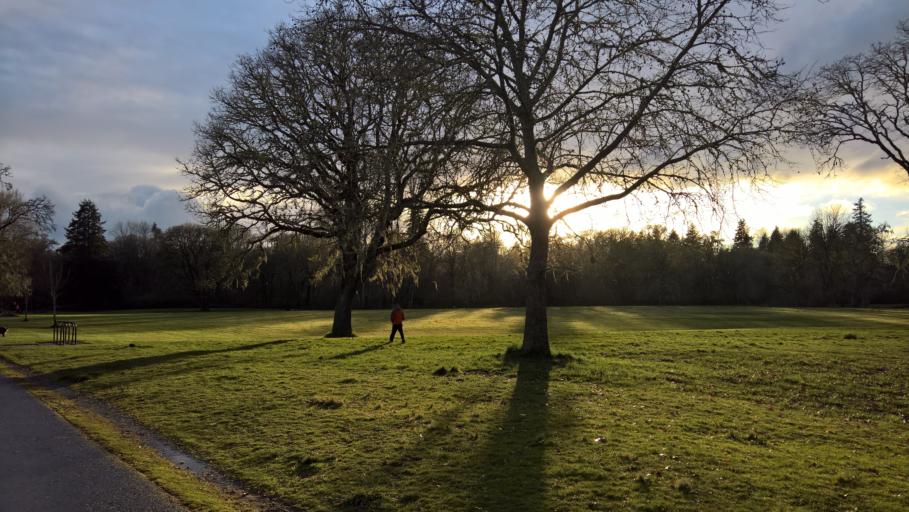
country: US
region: Oregon
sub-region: Benton County
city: Corvallis
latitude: 44.5386
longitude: -123.2478
